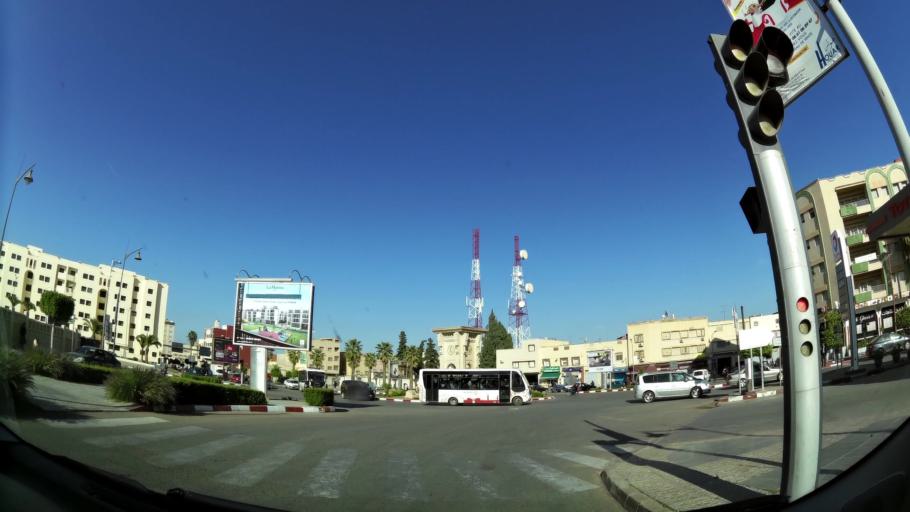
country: MA
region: Oriental
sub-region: Oujda-Angad
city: Oujda
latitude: 34.6919
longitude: -1.9079
